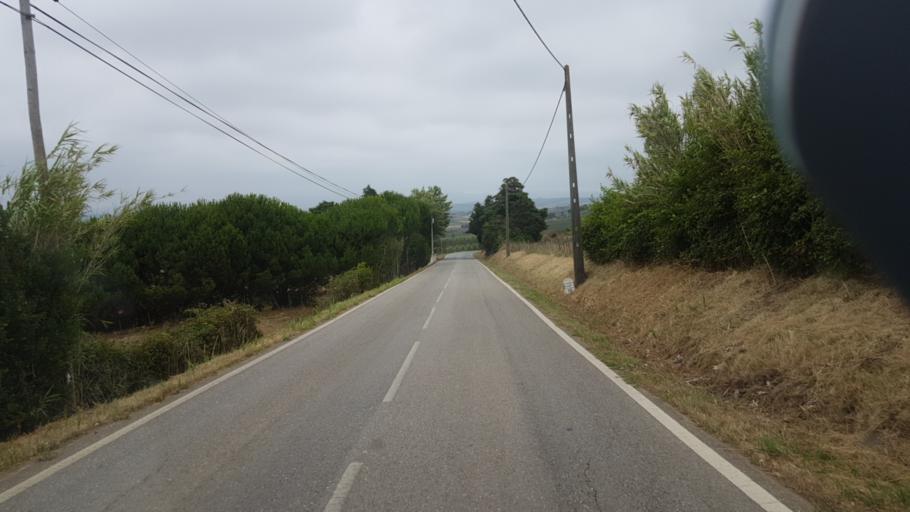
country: PT
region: Leiria
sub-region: Bombarral
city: Bombarral
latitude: 39.2776
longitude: -9.1866
